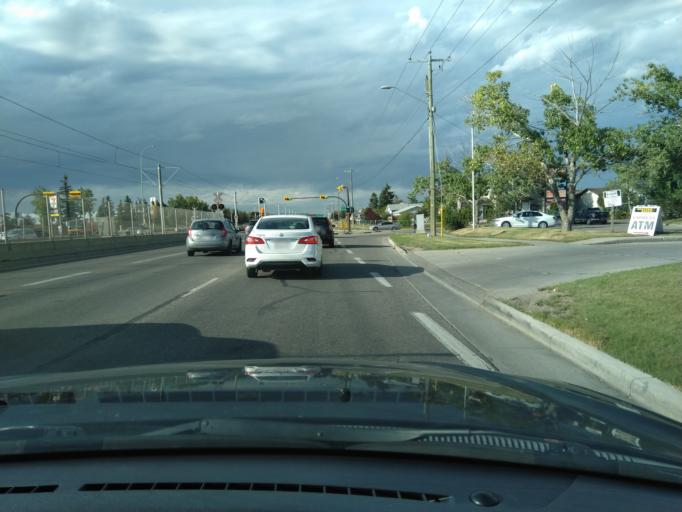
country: CA
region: Alberta
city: Calgary
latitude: 51.0877
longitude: -113.9815
